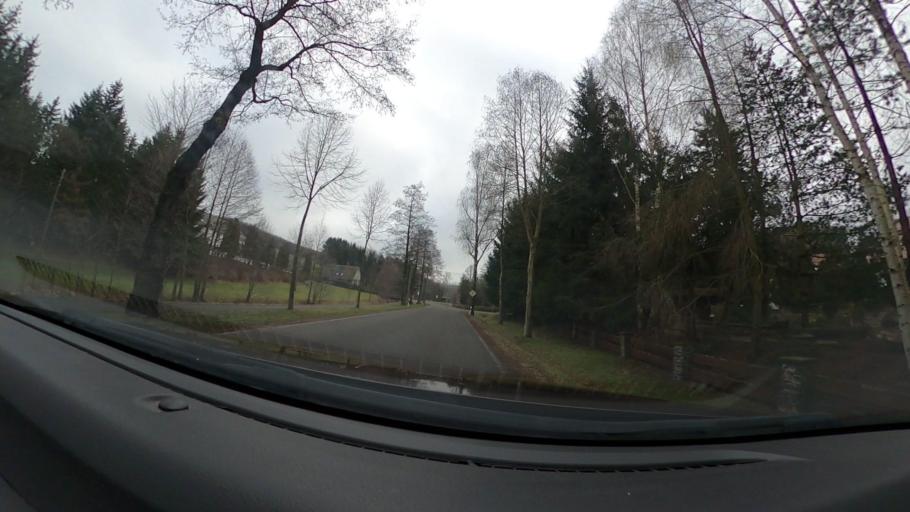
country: DE
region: Saxony
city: Oberschona
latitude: 50.8897
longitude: 13.2714
